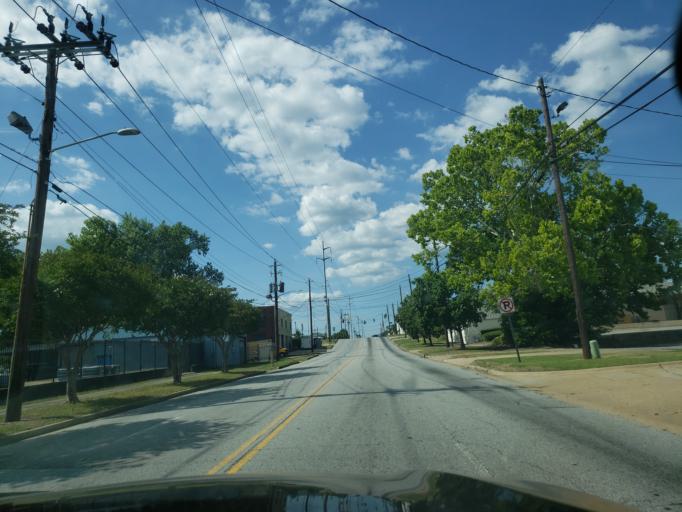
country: US
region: Georgia
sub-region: Muscogee County
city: Columbus
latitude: 32.4689
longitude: -84.9798
